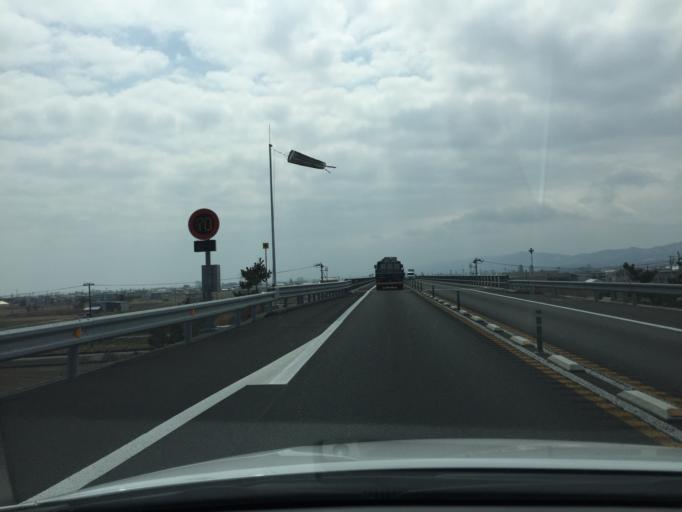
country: JP
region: Miyagi
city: Watari
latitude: 38.0353
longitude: 140.8919
